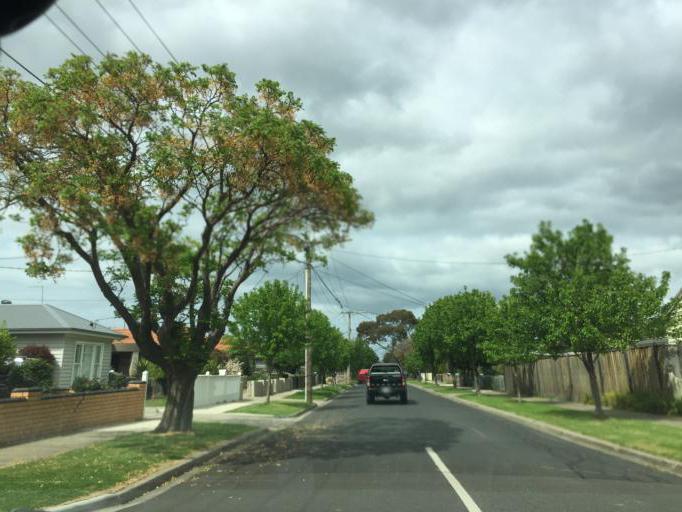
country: AU
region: Victoria
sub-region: Hobsons Bay
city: South Kingsville
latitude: -37.8167
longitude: 144.8675
